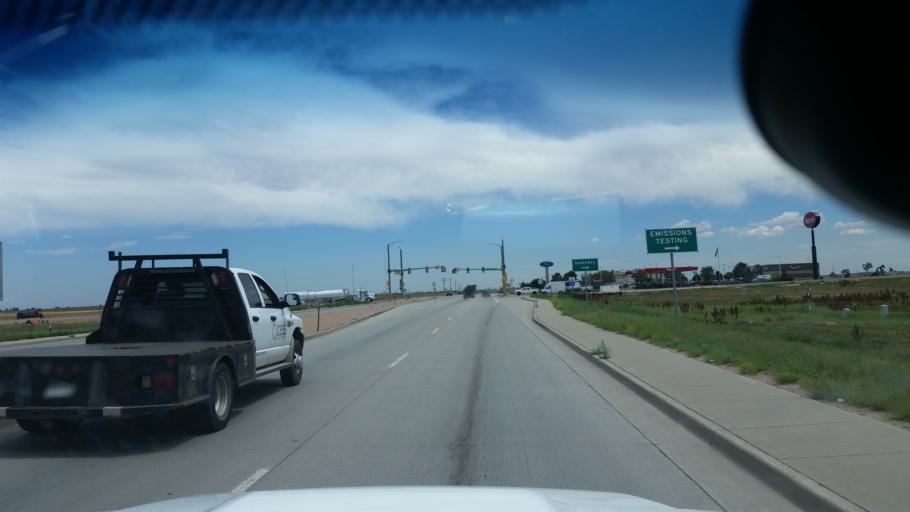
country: US
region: Colorado
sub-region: Weld County
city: Dacono
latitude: 40.0876
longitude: -104.9773
